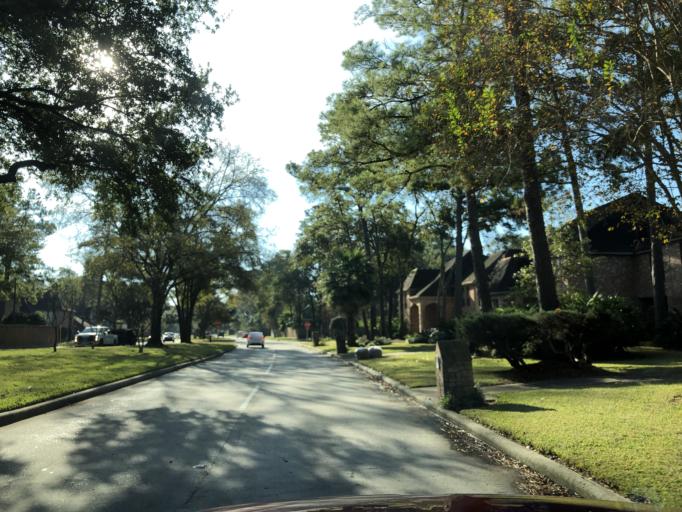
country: US
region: Texas
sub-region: Harris County
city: Tomball
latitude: 30.0300
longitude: -95.5533
